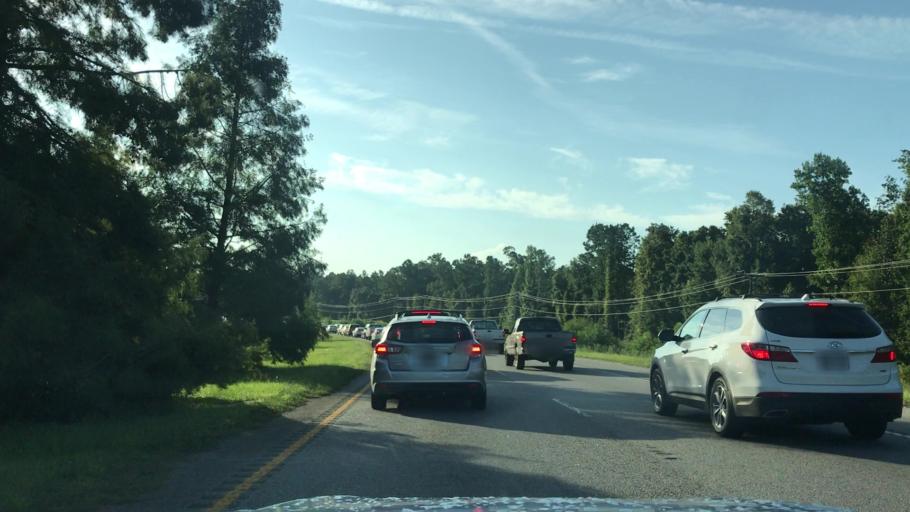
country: US
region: South Carolina
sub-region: Charleston County
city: Shell Point
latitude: 32.8118
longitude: -80.0574
